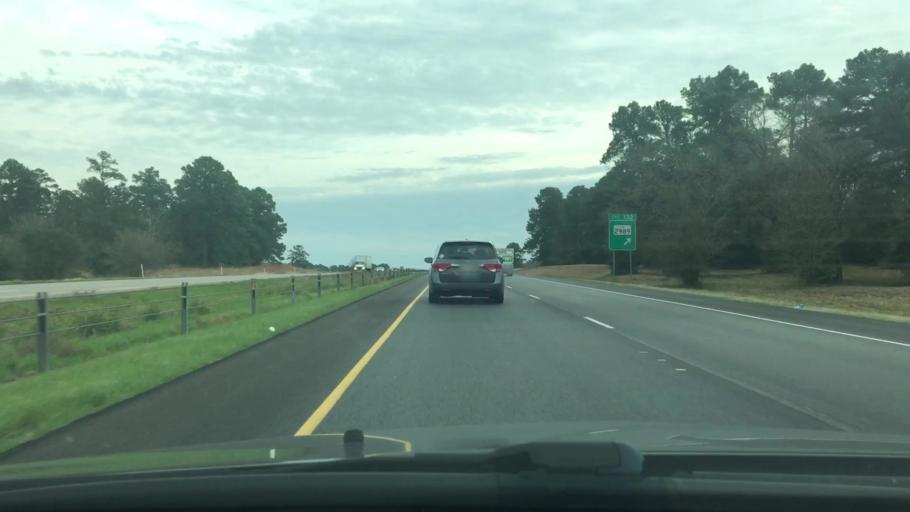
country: US
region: Texas
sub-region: Madison County
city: Madisonville
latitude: 30.8785
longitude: -95.7646
